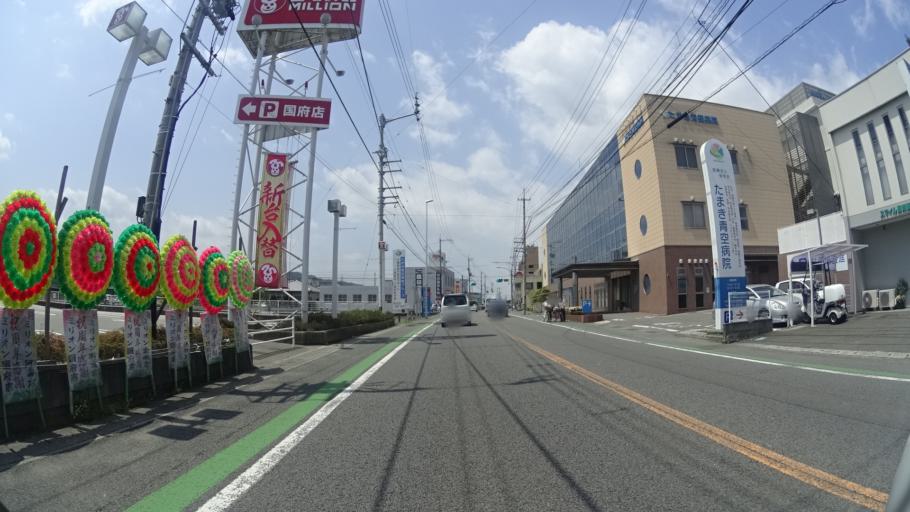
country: JP
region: Tokushima
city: Ishii
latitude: 34.0721
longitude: 134.4865
